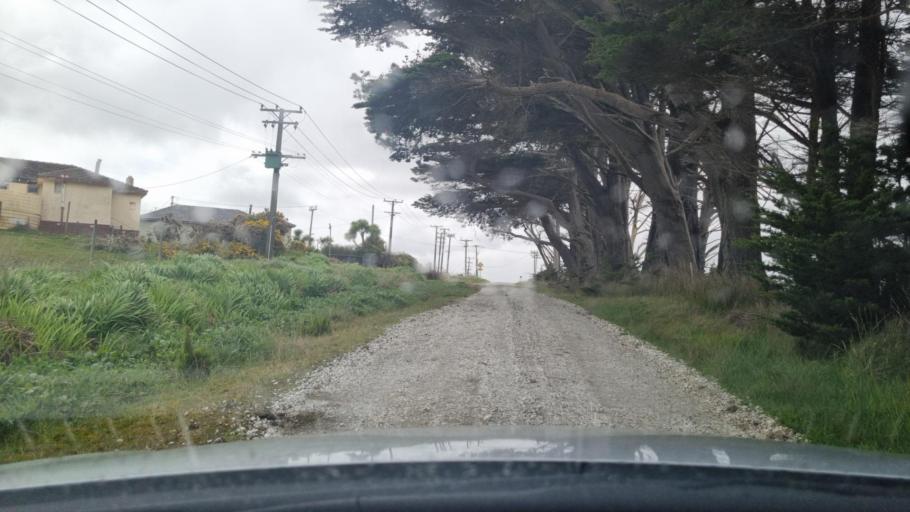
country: NZ
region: Southland
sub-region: Invercargill City
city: Bluff
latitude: -46.5861
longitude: 168.3031
